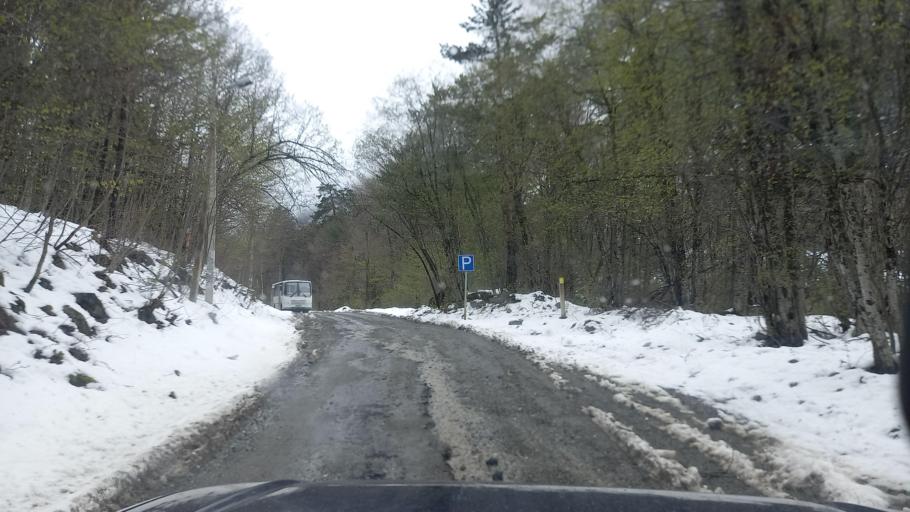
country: RU
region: North Ossetia
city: Mizur
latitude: 42.7894
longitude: 43.9065
